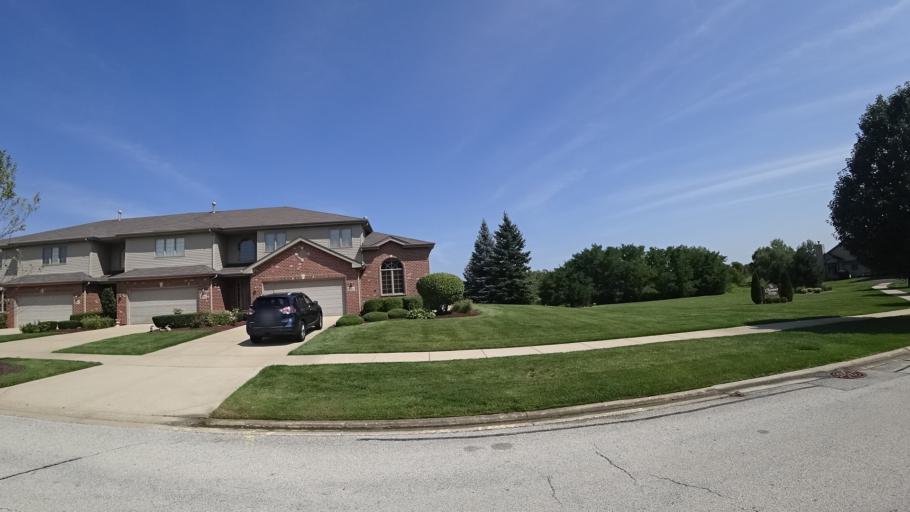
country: US
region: Illinois
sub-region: Cook County
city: Orland Hills
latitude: 41.5633
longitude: -87.8437
